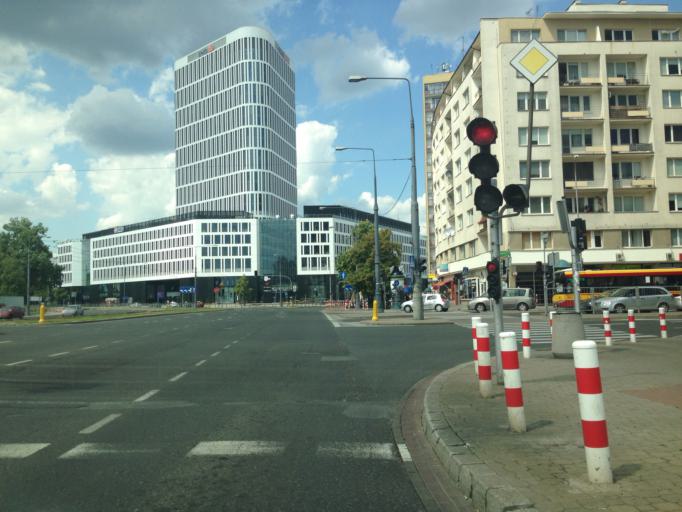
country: PL
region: Masovian Voivodeship
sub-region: Warszawa
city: Srodmiescie
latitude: 52.2106
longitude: 21.0210
